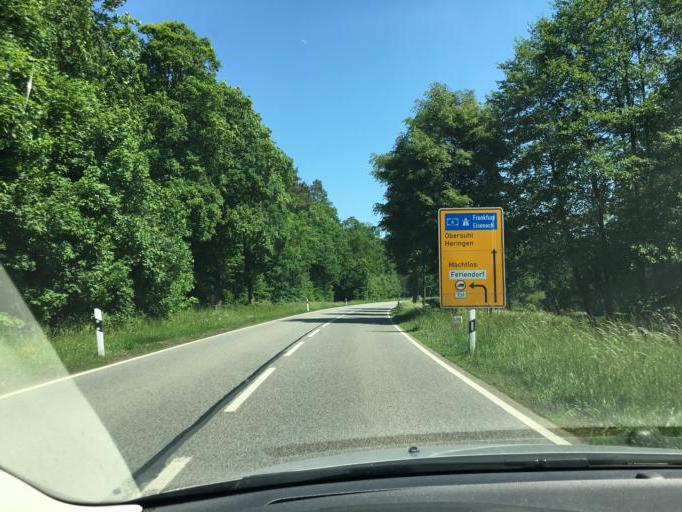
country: DE
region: Hesse
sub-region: Regierungsbezirk Kassel
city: Ronshausen
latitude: 50.9444
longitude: 9.8864
